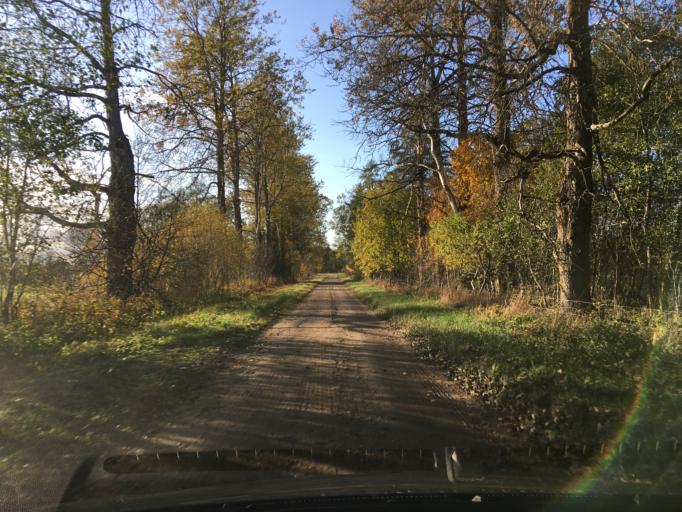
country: EE
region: Laeaene
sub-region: Lihula vald
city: Lihula
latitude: 58.5649
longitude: 23.7896
